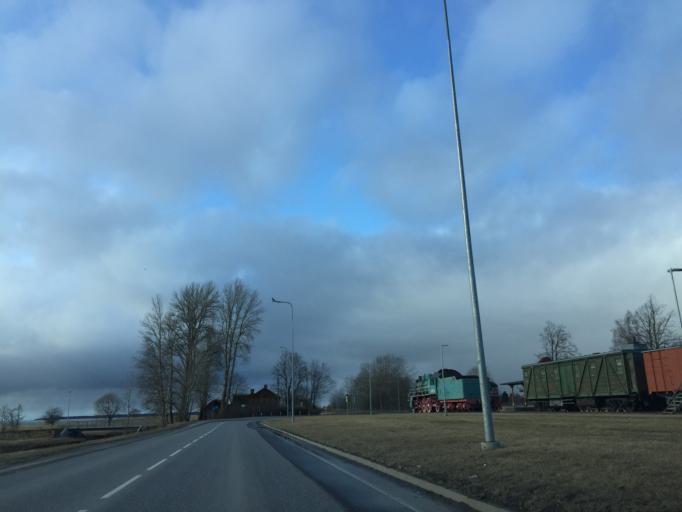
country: EE
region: Laeaene
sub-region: Haapsalu linn
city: Haapsalu
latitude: 58.9382
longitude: 23.5311
